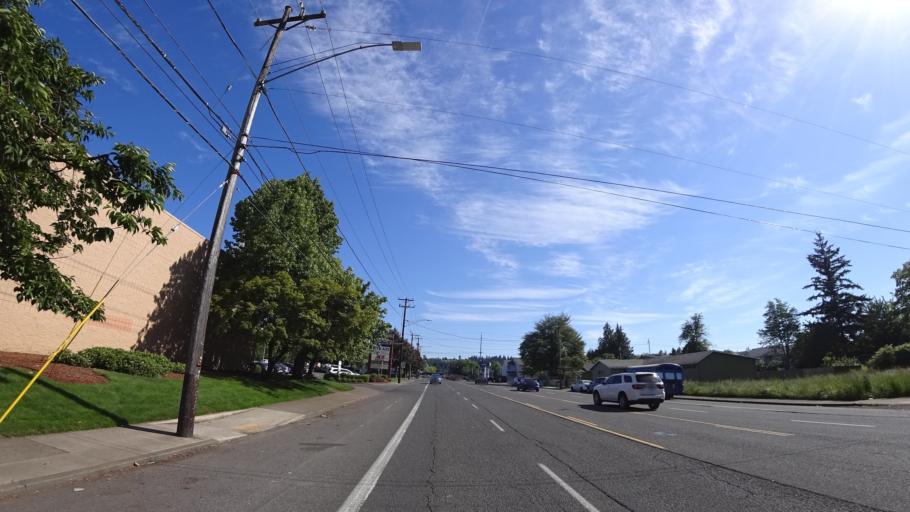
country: US
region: Oregon
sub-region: Multnomah County
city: Gresham
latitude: 45.5061
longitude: -122.4966
